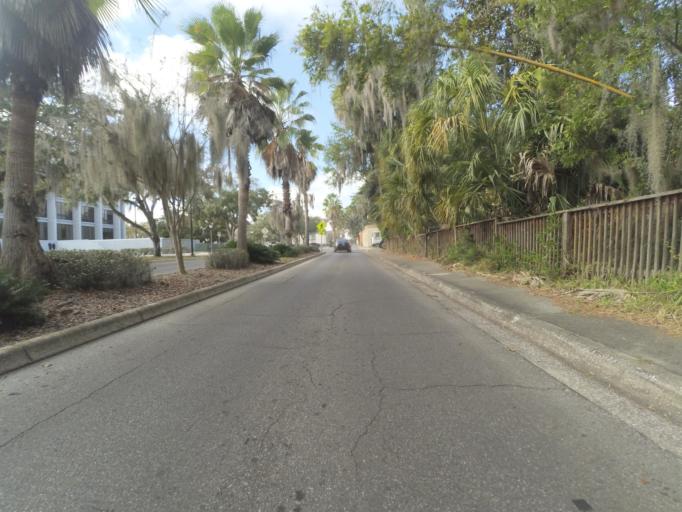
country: US
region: Florida
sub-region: Alachua County
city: Gainesville
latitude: 29.6535
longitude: -82.3223
